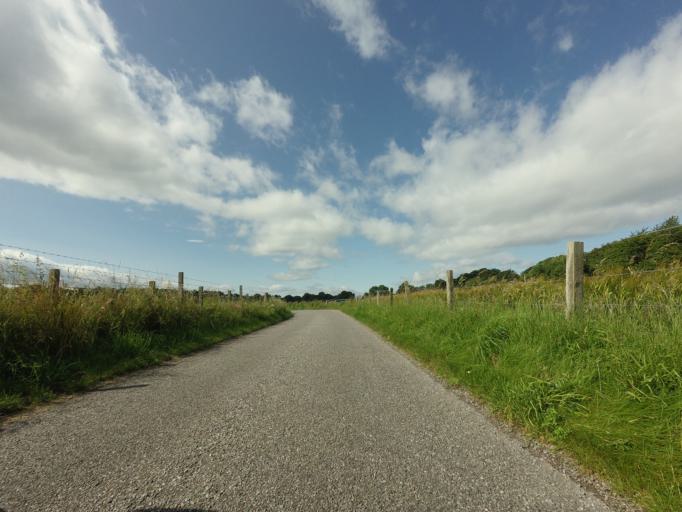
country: GB
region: Scotland
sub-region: Highland
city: Nairn
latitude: 57.5717
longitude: -3.8671
